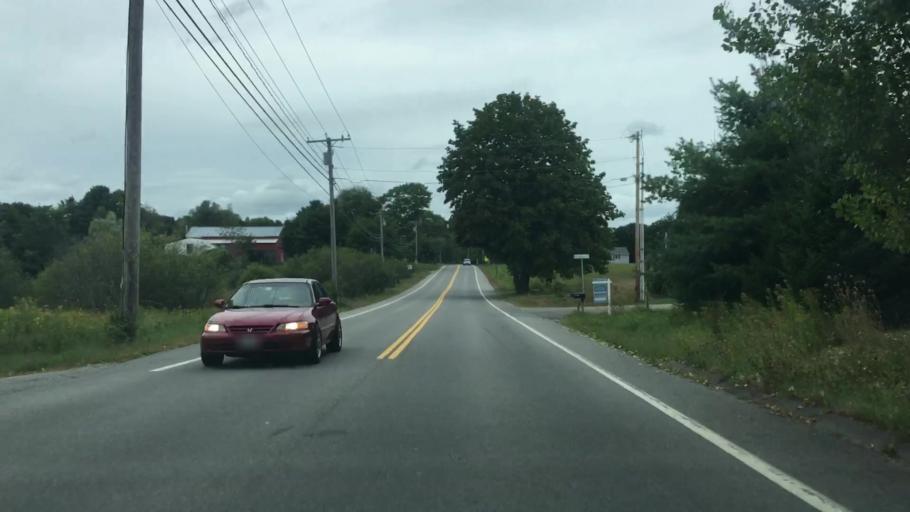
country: US
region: Maine
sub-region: Cumberland County
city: Yarmouth
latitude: 43.8272
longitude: -70.1946
